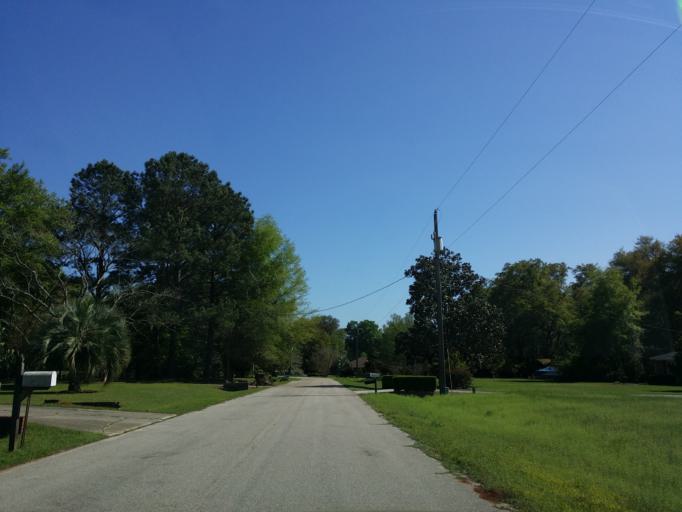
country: US
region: Florida
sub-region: Leon County
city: Tallahassee
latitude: 30.4823
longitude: -84.1856
